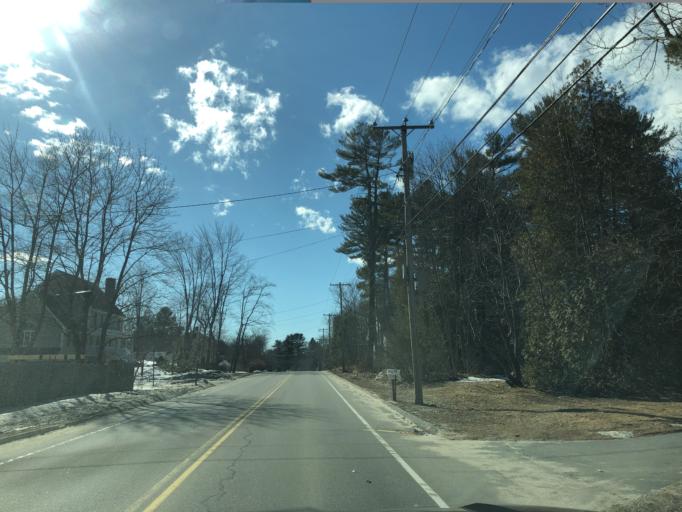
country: US
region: Maine
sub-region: Cumberland County
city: Falmouth
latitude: 43.7136
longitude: -70.2684
